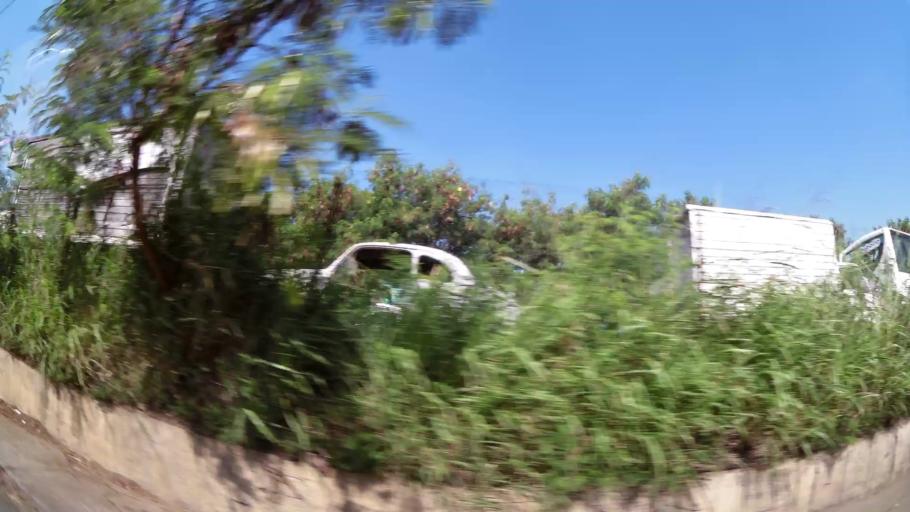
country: CO
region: Valle del Cauca
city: Cali
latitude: 3.4181
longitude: -76.5212
